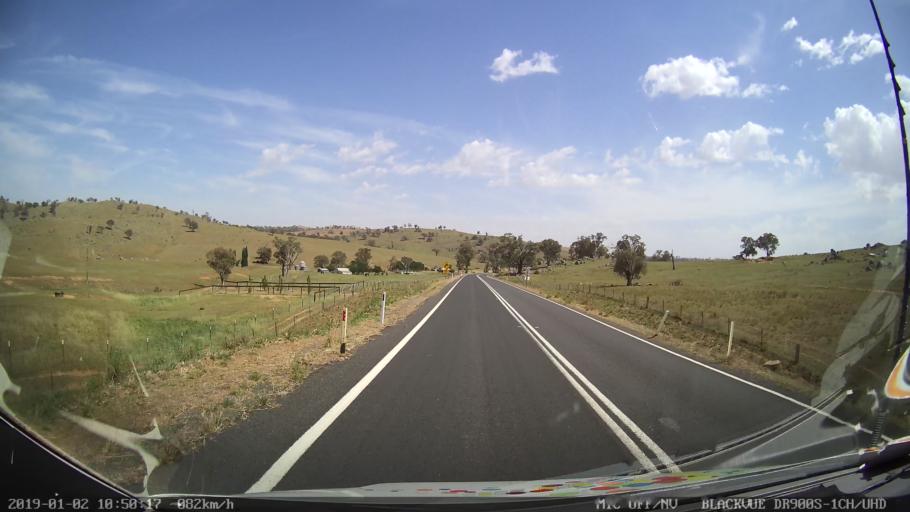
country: AU
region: New South Wales
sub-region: Cootamundra
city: Cootamundra
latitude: -34.7155
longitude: 148.2767
